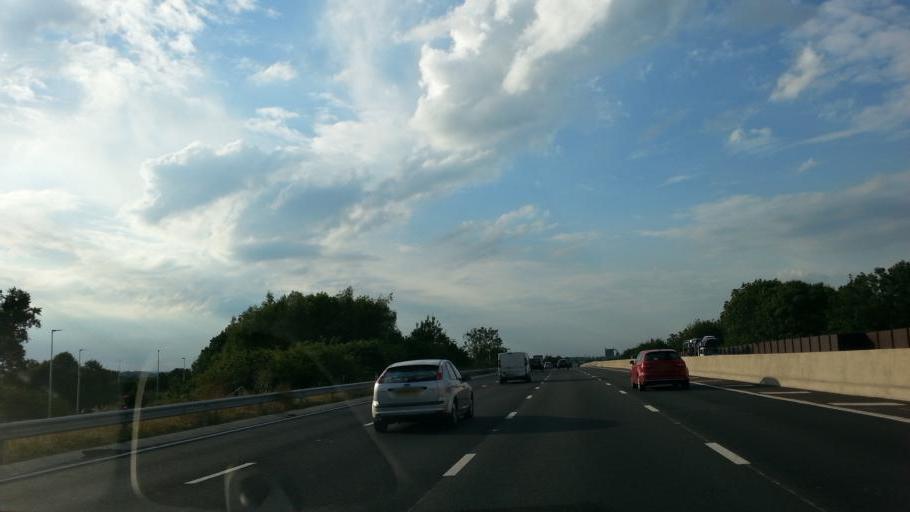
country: GB
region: England
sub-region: Worcestershire
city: Droitwich
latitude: 52.2860
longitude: -2.1195
